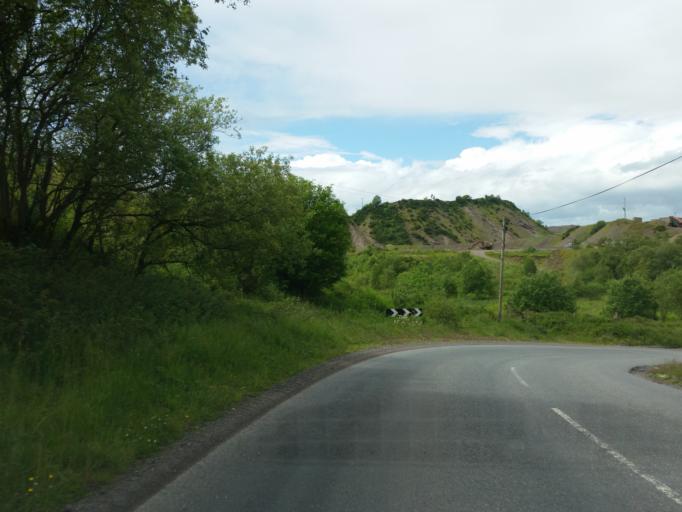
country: GB
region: Northern Ireland
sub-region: Omagh District
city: Omagh
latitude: 54.5099
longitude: -7.0582
